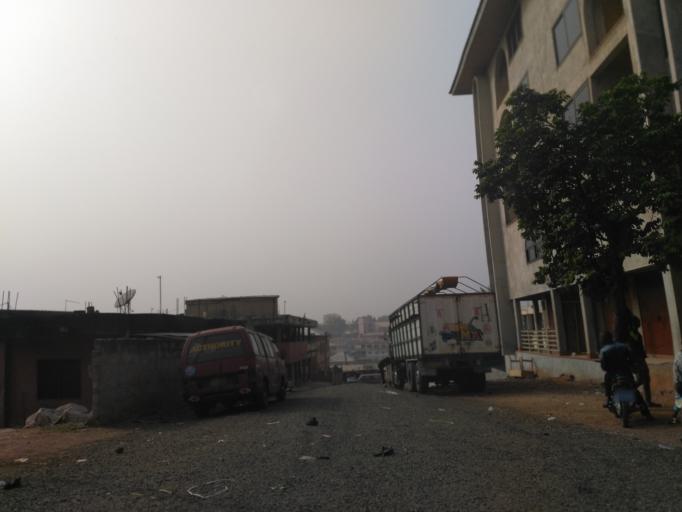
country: GH
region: Ashanti
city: Kumasi
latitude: 6.6982
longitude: -1.6115
